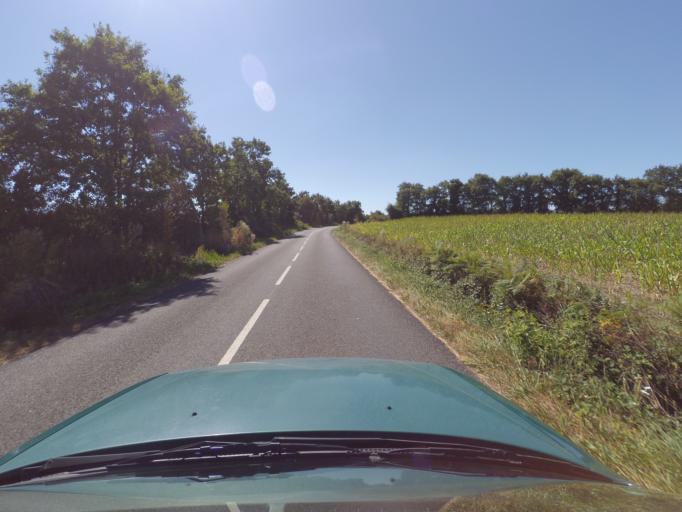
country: FR
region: Pays de la Loire
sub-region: Departement de la Loire-Atlantique
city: Le Bignon
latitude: 47.1047
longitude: -1.4954
